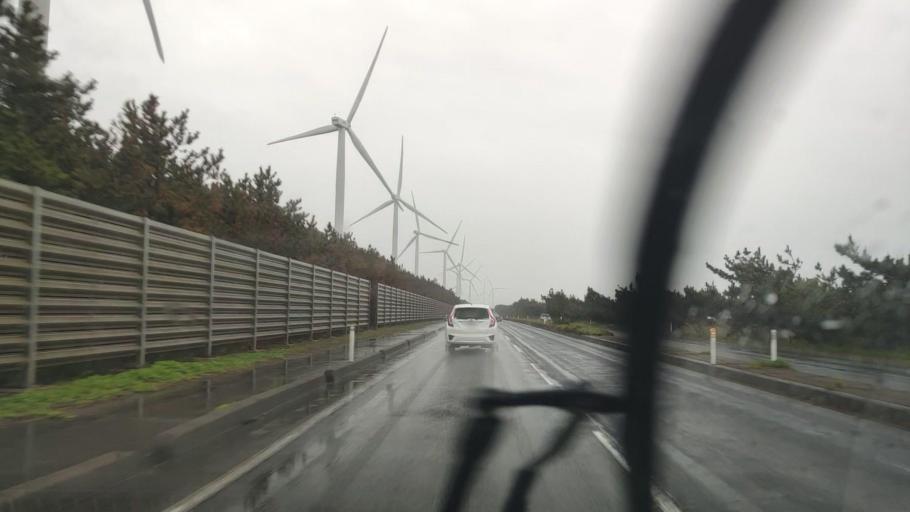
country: JP
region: Akita
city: Tenno
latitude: 39.8115
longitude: 140.0316
